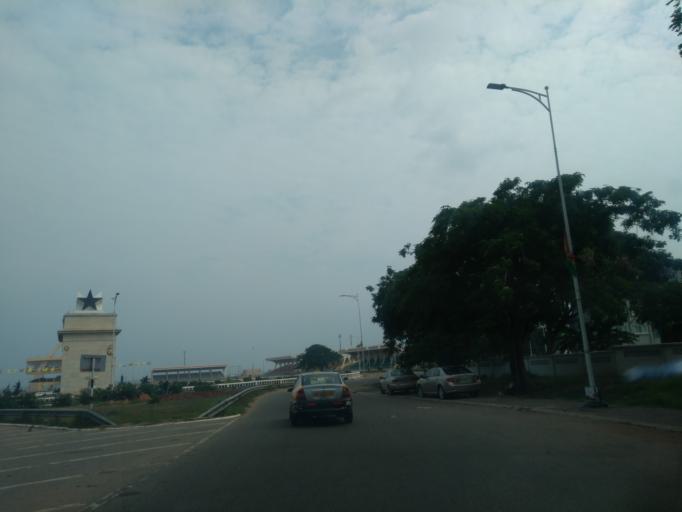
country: GH
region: Greater Accra
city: Accra
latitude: 5.5501
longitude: -0.1930
